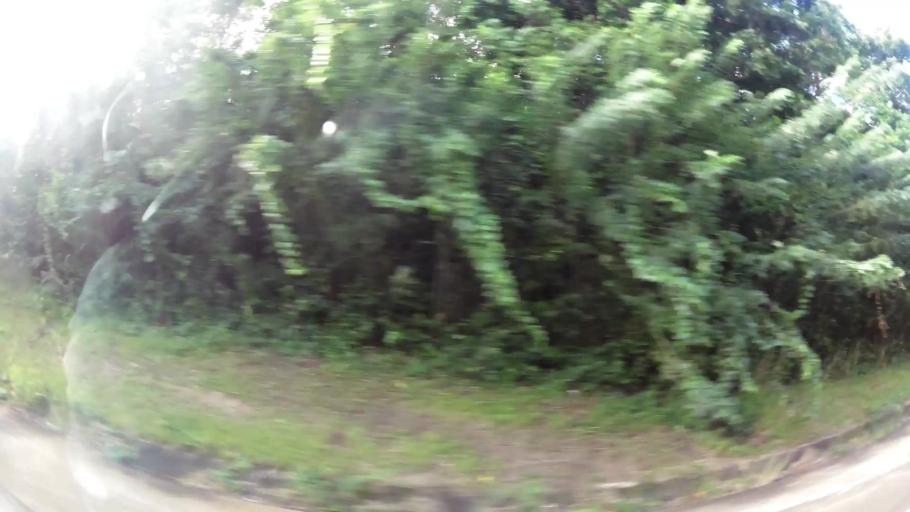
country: MQ
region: Martinique
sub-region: Martinique
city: Ducos
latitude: 14.5995
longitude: -60.9475
